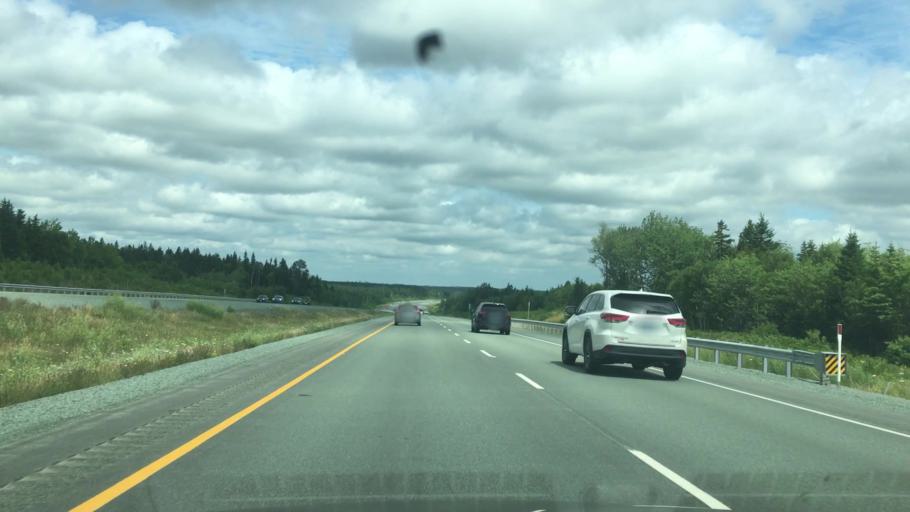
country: CA
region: Nova Scotia
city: Oxford
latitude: 45.6338
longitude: -63.7444
